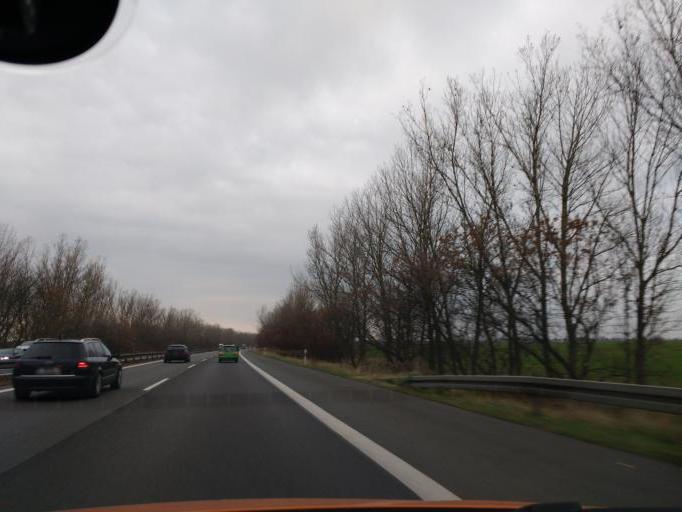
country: DE
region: Brandenburg
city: Fehrbellin
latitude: 52.7785
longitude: 12.8060
